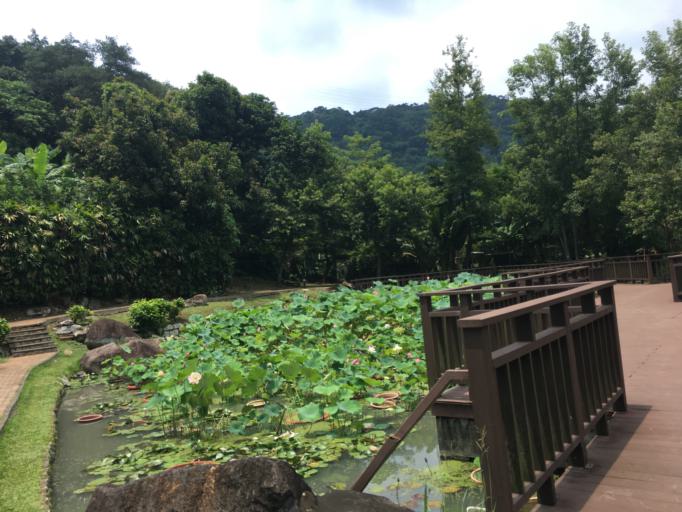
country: TW
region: Taipei
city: Taipei
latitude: 25.0992
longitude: 121.5466
